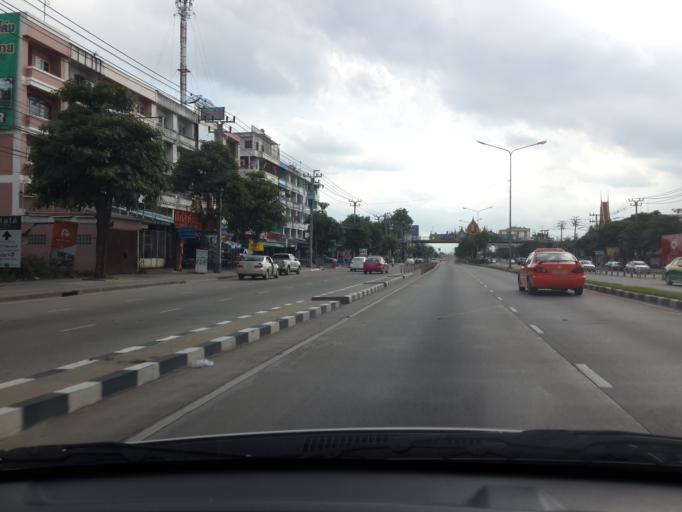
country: TH
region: Bangkok
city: Min Buri
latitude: 13.7982
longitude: 100.7128
